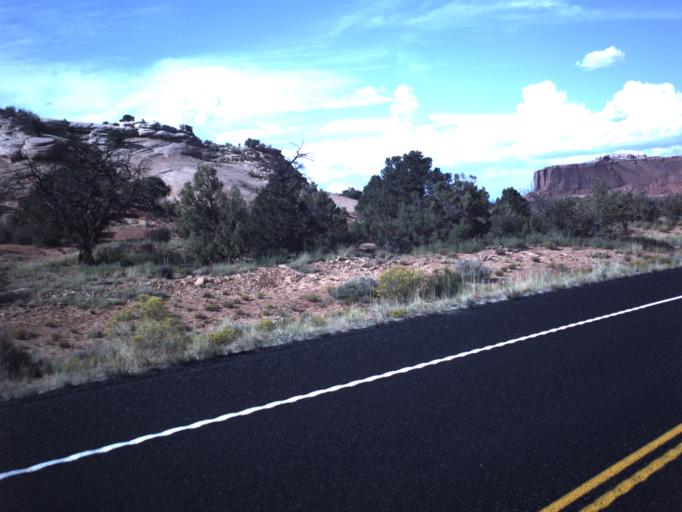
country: US
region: Utah
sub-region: Grand County
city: Moab
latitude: 38.6393
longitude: -109.7508
